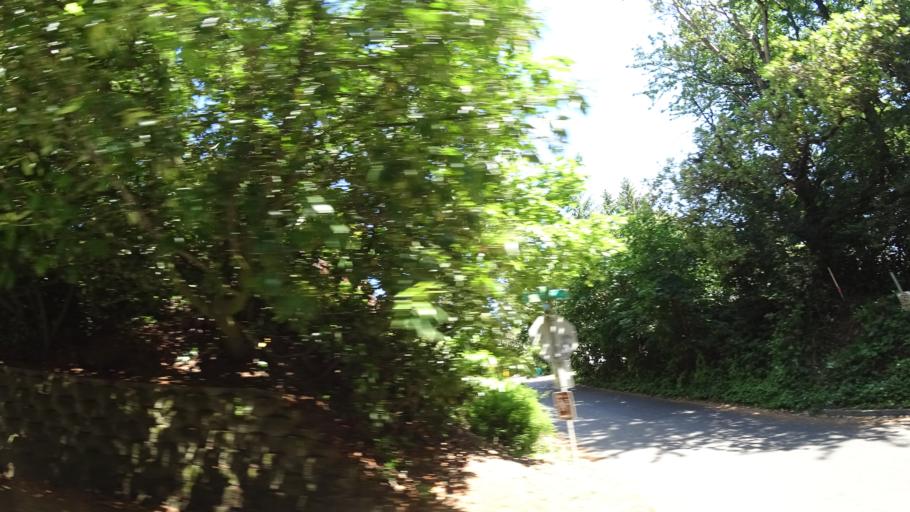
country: US
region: Oregon
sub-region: Washington County
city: Garden Home-Whitford
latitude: 45.4725
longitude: -122.7077
